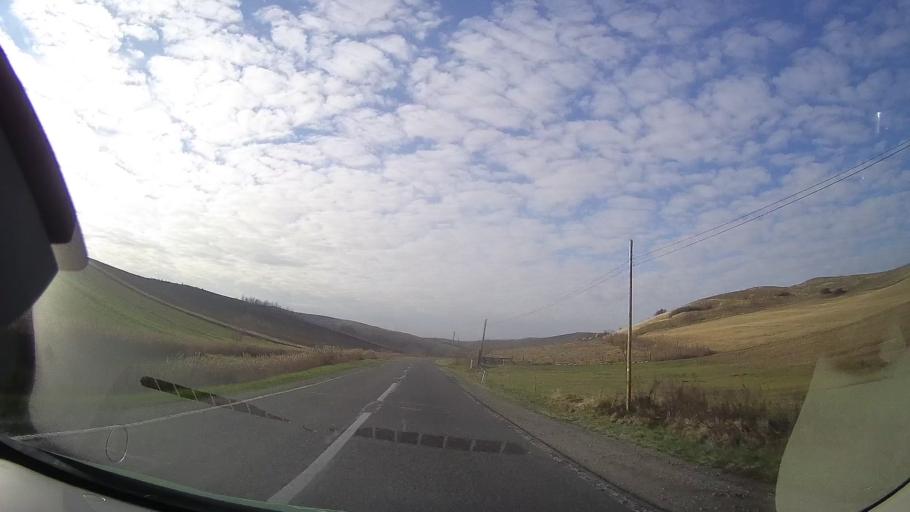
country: RO
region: Cluj
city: Jucu Herghelia
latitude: 46.8116
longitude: 23.8248
